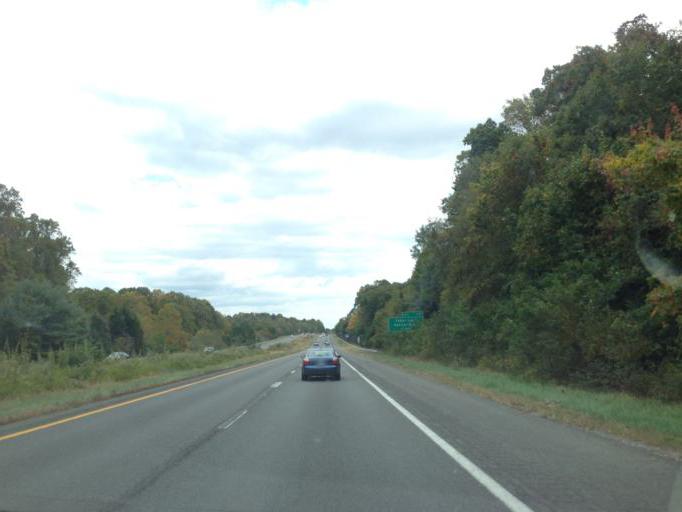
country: US
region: Maryland
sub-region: Howard County
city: Riverside
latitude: 39.1944
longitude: -76.9194
